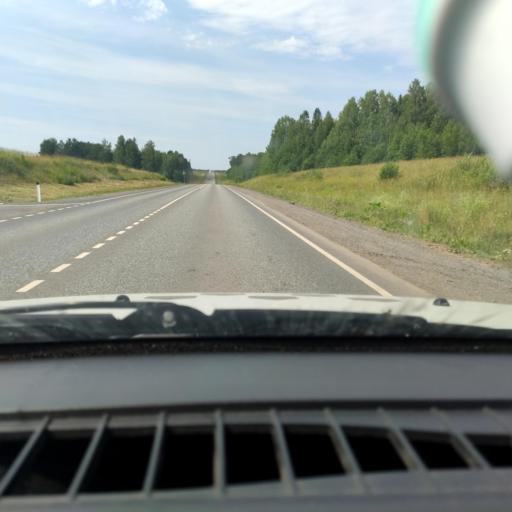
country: RU
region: Perm
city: Siva
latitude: 58.5165
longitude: 54.0152
